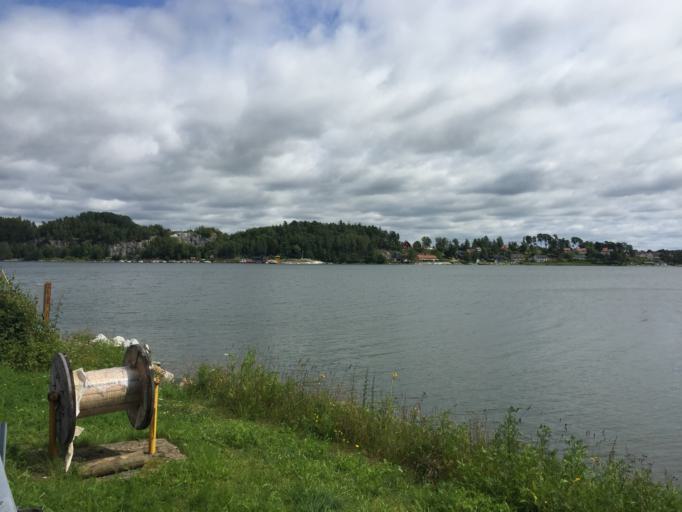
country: SE
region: Soedermanland
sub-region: Trosa Kommun
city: Trosa
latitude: 58.9703
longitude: 17.7026
